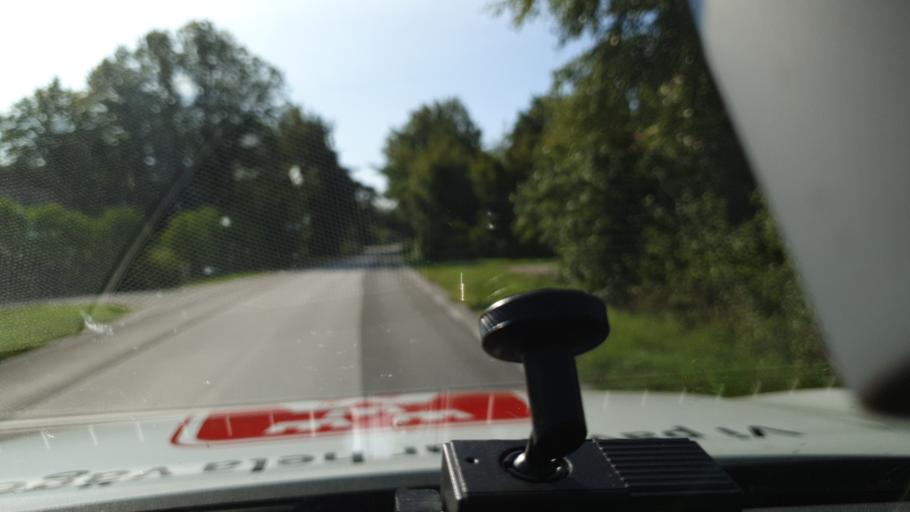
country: SE
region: Gotland
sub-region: Gotland
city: Hemse
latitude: 57.0952
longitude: 18.3039
